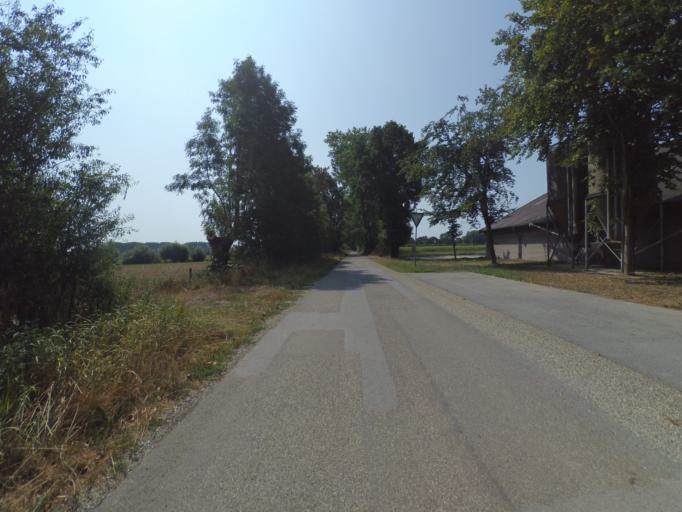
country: DE
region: North Rhine-Westphalia
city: Rees
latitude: 51.7909
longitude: 6.4150
